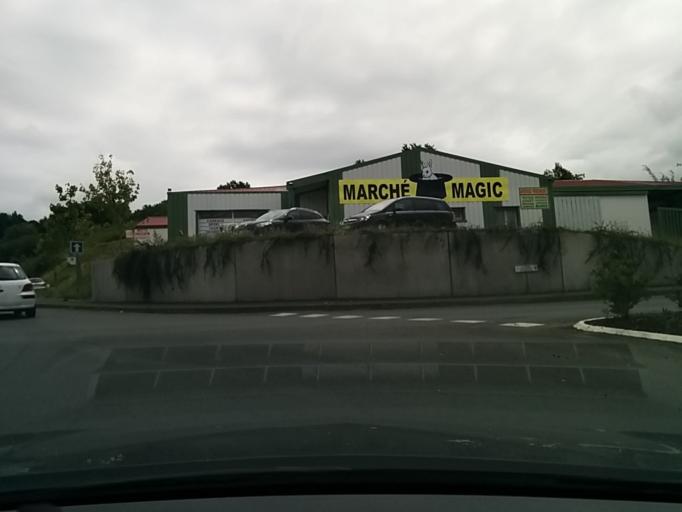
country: FR
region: Aquitaine
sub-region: Departement des Pyrenees-Atlantiques
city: Cambo-les-Bains
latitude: 43.3509
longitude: -1.4167
